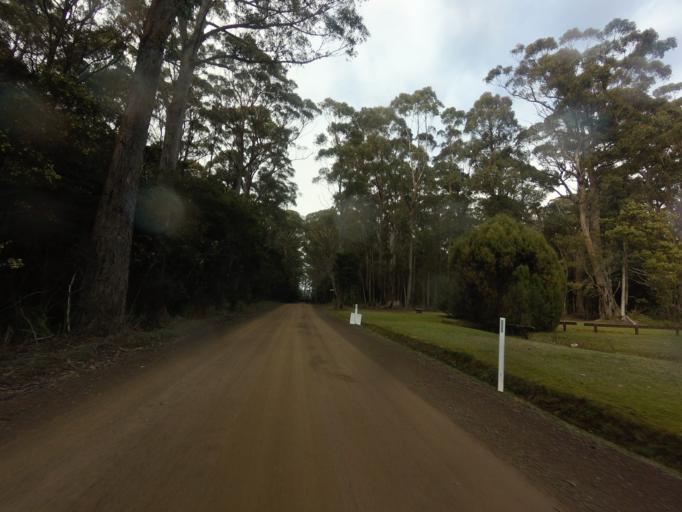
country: AU
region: Tasmania
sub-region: Huon Valley
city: Geeveston
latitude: -43.5397
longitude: 146.8921
